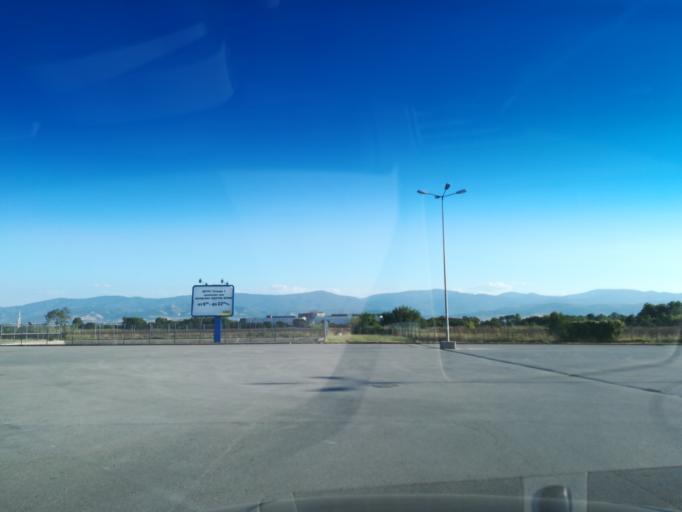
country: BG
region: Plovdiv
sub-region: Obshtina Plovdiv
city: Plovdiv
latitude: 42.1588
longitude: 24.6790
